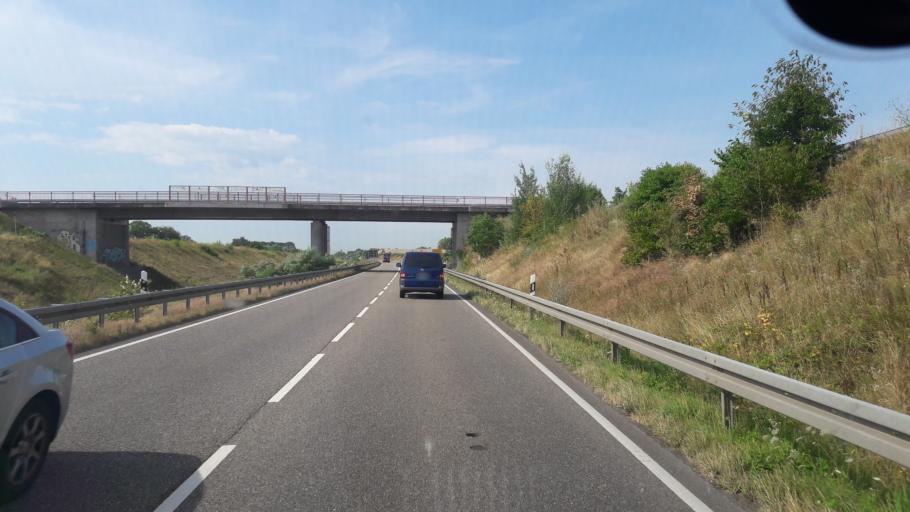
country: DE
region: Baden-Wuerttemberg
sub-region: Karlsruhe Region
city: Durmersheim
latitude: 48.9375
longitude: 8.2842
